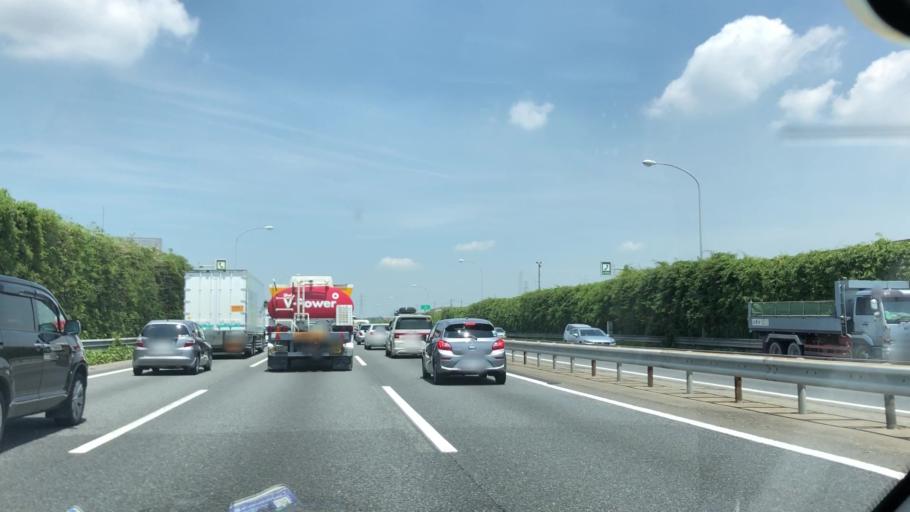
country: JP
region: Saitama
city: Iwatsuki
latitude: 35.9181
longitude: 139.7054
